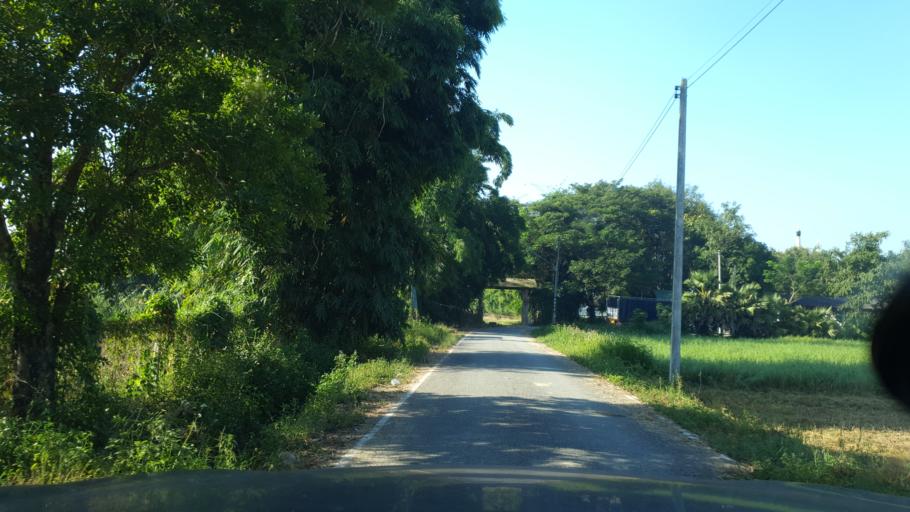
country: TH
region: Lamphun
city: Ban Thi
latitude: 18.6862
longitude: 99.1508
